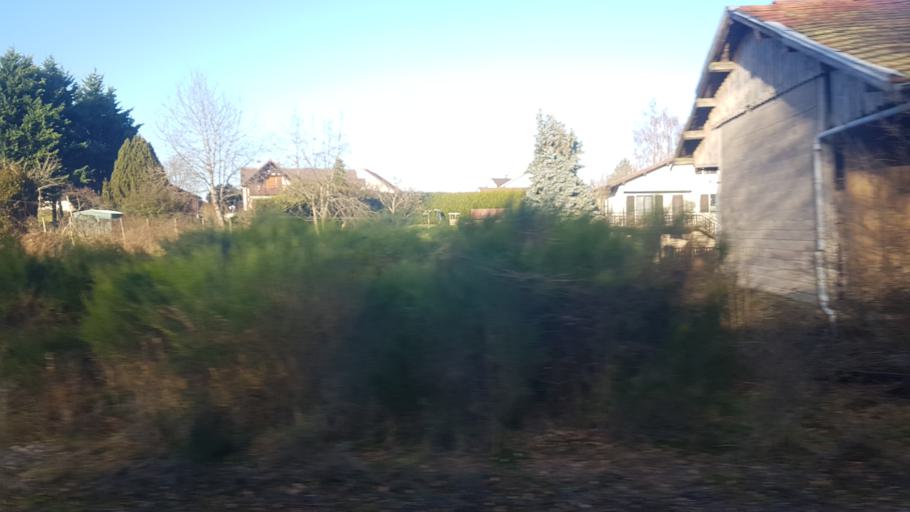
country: FR
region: Lorraine
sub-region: Departement des Vosges
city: Hadol
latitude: 48.0949
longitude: 6.4425
